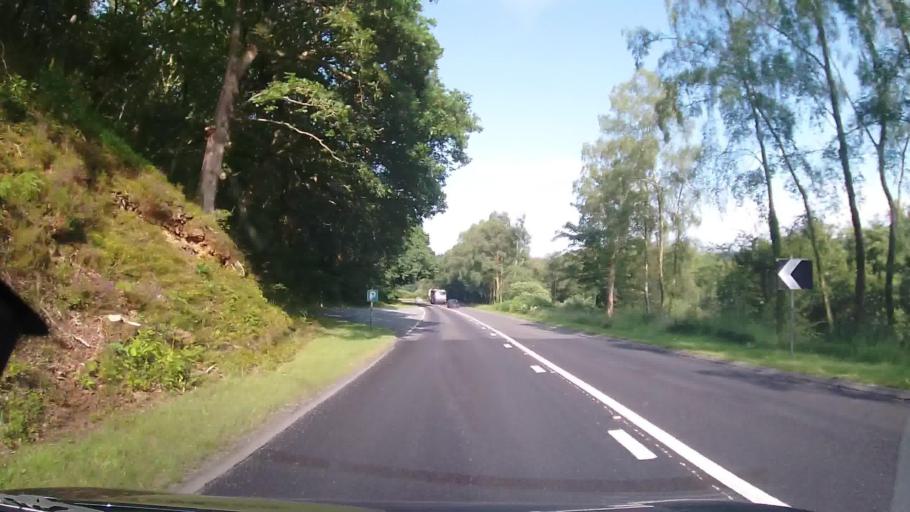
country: GB
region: Wales
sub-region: Gwynedd
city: Penrhyndeudraeth
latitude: 52.9414
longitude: -4.0398
